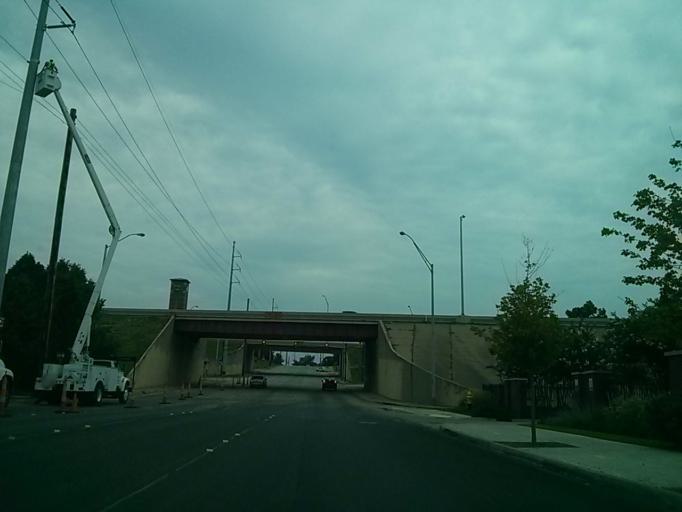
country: US
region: Oklahoma
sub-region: Tulsa County
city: Tulsa
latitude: 36.1610
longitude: -95.9908
